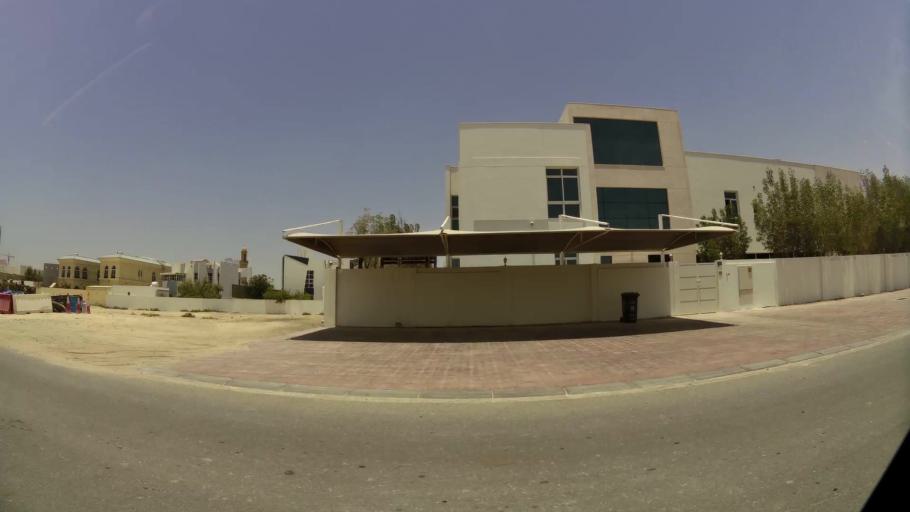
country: AE
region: Dubai
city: Dubai
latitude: 25.0975
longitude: 55.1860
